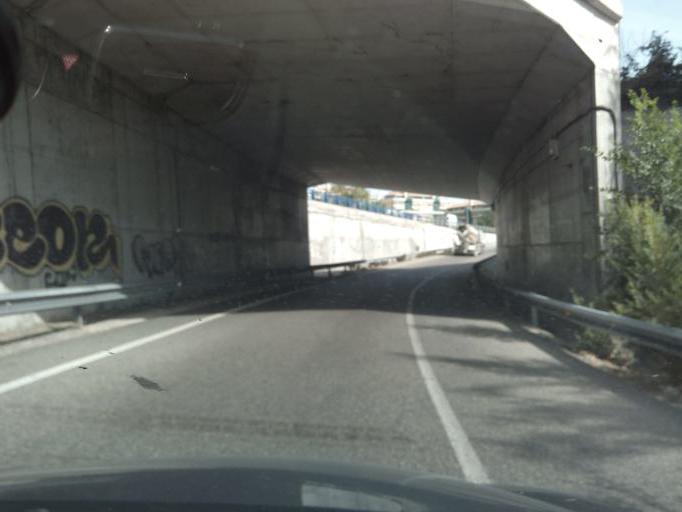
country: ES
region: Madrid
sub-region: Provincia de Madrid
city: Barajas de Madrid
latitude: 40.4515
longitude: -3.5863
